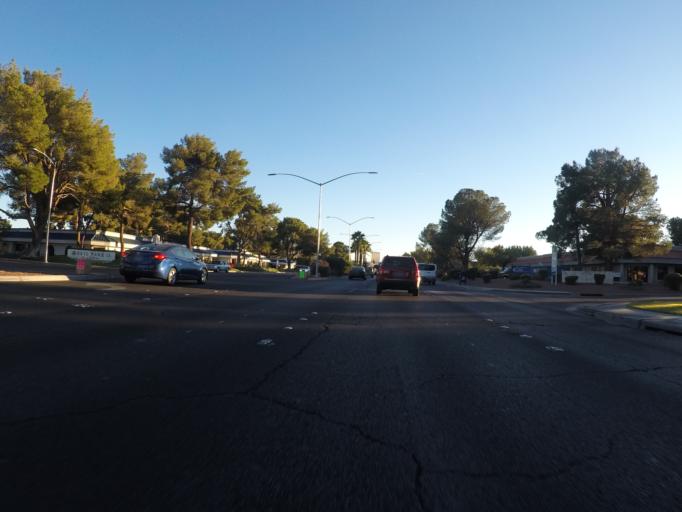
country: US
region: Nevada
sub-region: Clark County
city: Las Vegas
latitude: 36.1645
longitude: -115.1727
